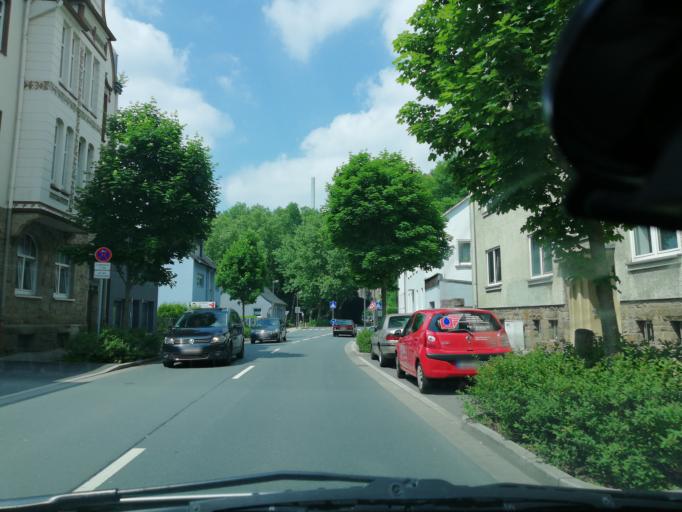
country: DE
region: North Rhine-Westphalia
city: Herdecke
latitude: 51.4007
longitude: 7.4261
